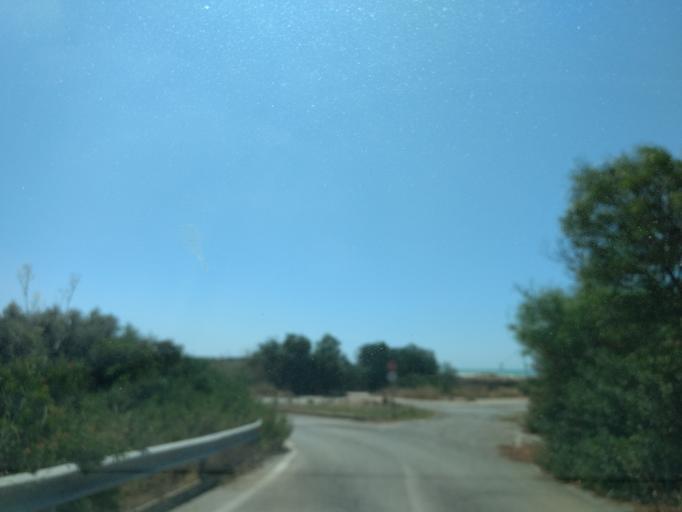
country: IT
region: Sicily
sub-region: Ragusa
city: Pozzallo
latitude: 36.7188
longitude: 14.8152
